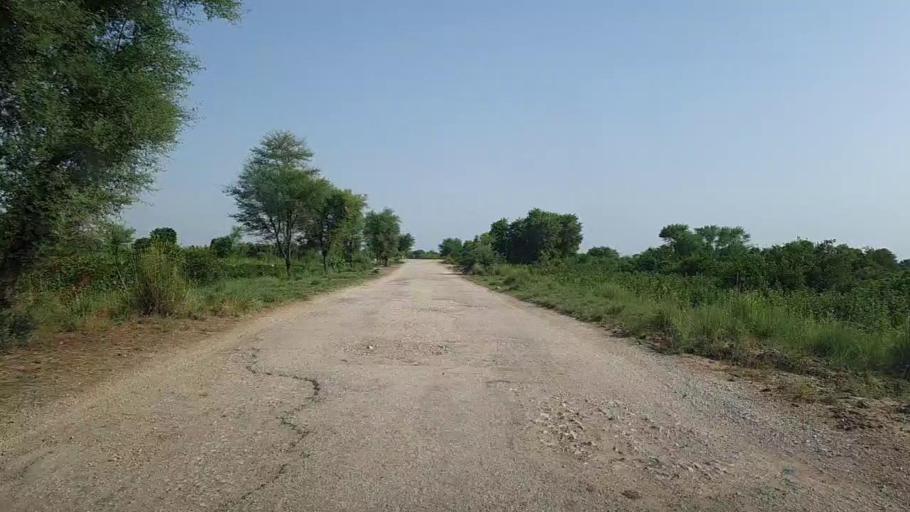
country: PK
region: Sindh
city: Karaundi
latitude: 26.8716
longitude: 68.3288
